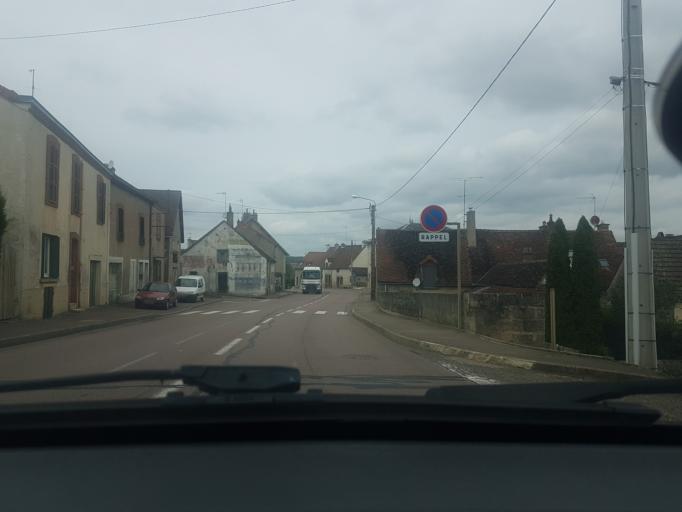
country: FR
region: Bourgogne
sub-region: Departement de la Cote-d'Or
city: Arnay-le-Duc
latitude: 47.1332
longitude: 4.4883
